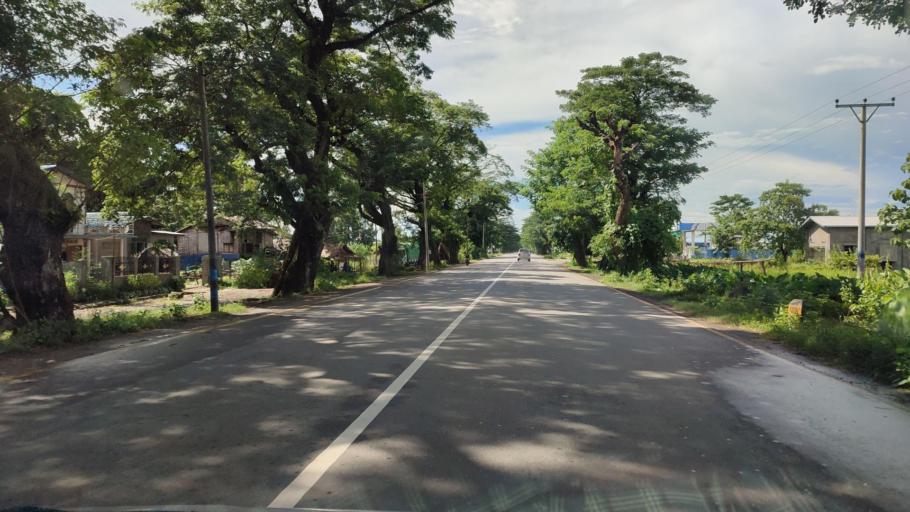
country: MM
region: Bago
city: Pyu
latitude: 18.2584
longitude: 96.5301
